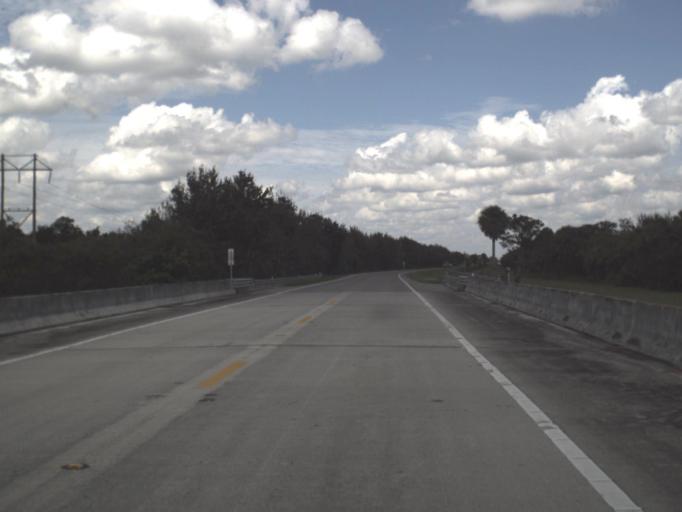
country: US
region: Florida
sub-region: Collier County
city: Immokalee
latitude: 26.2034
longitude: -81.3462
